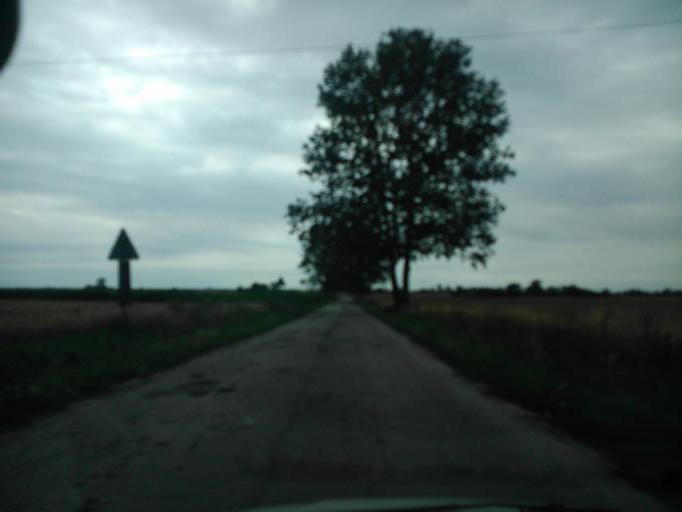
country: PL
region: Kujawsko-Pomorskie
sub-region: Powiat brodnicki
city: Brodnica
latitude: 53.2925
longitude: 19.3403
